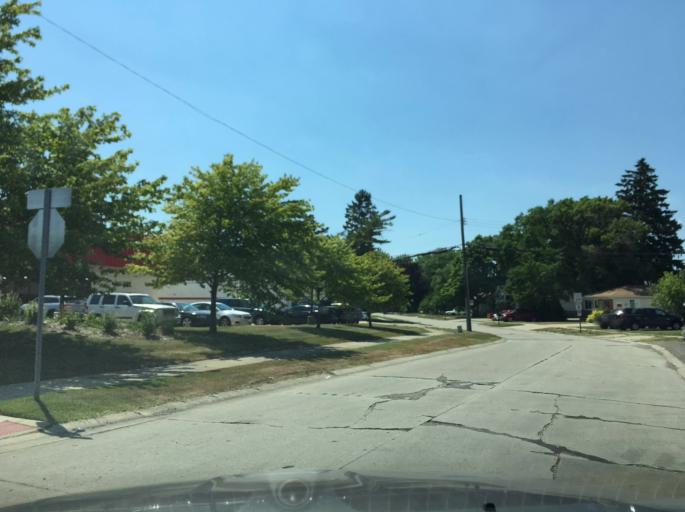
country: US
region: Michigan
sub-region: Macomb County
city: Fraser
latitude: 42.5443
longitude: -82.9064
